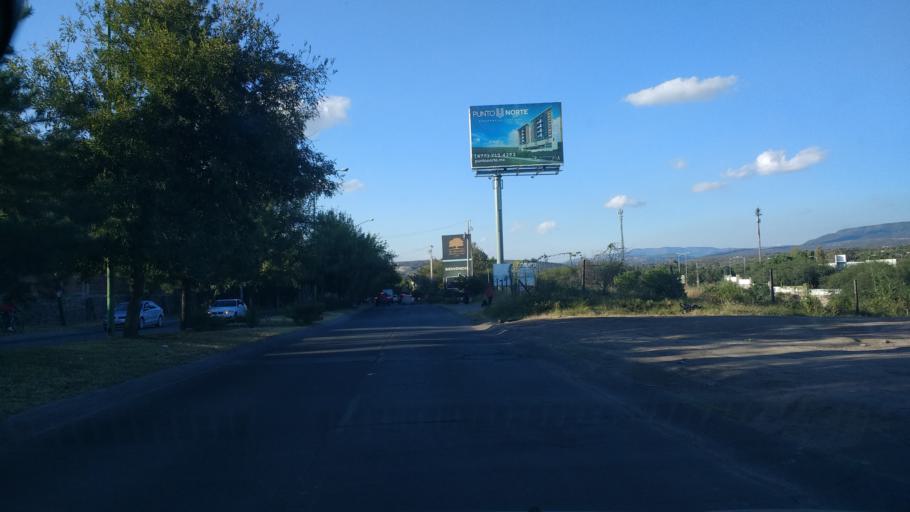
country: MX
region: Guanajuato
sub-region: Leon
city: La Ermita
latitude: 21.1797
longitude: -101.7039
